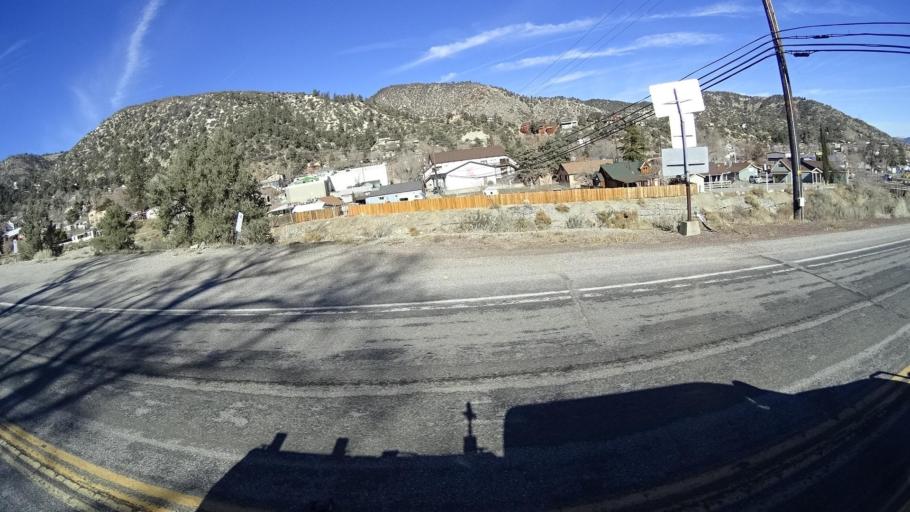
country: US
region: California
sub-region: Kern County
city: Frazier Park
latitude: 34.8205
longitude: -118.9466
